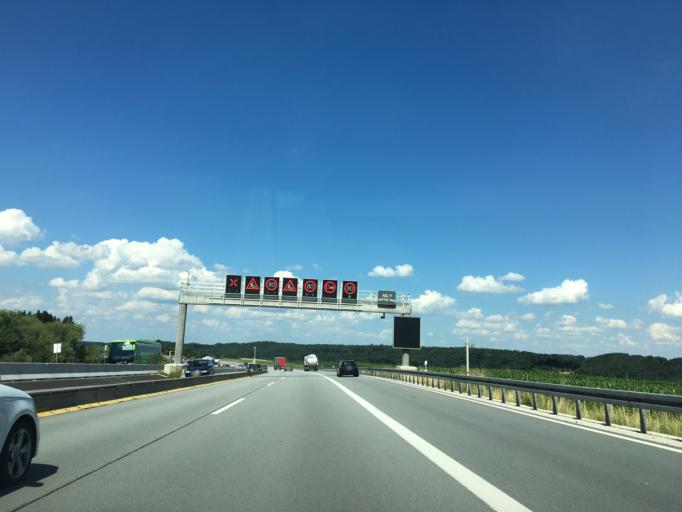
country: DE
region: Bavaria
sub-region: Upper Bavaria
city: Schweitenkirchen
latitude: 48.5307
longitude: 11.5920
